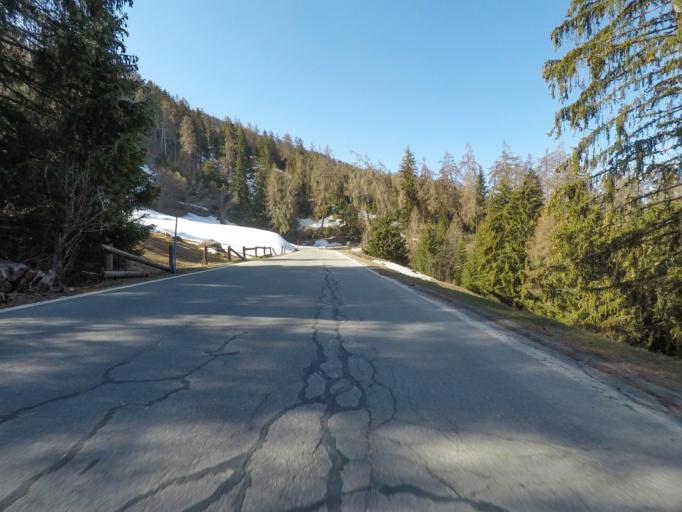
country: CH
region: Valais
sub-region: Sion District
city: Sitten
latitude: 46.1971
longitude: 7.3606
